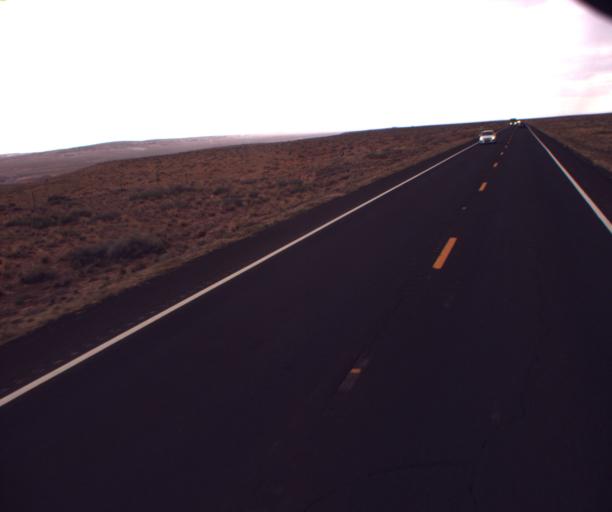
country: US
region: Arizona
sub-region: Coconino County
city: Tuba City
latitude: 36.1775
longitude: -111.0797
